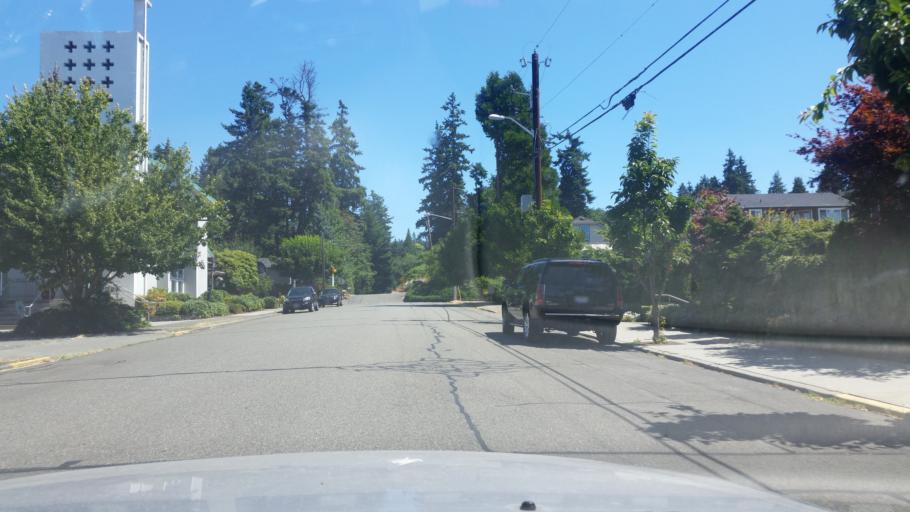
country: US
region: Washington
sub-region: Snohomish County
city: Edmonds
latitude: 47.8138
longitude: -122.3734
